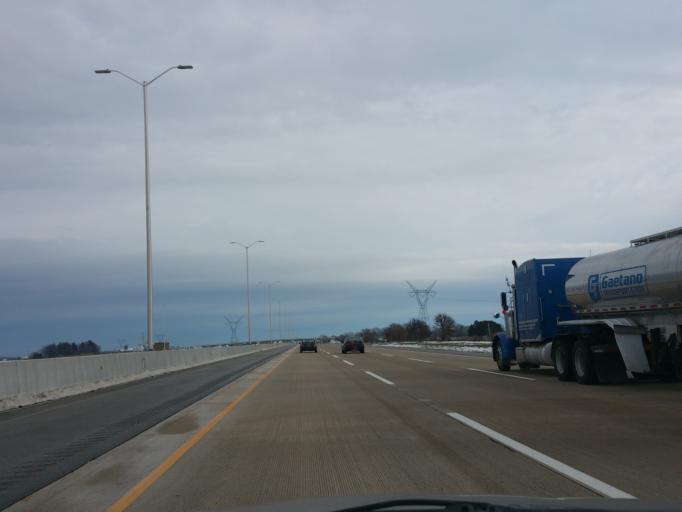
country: US
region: Illinois
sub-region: McHenry County
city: Marengo
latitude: 42.2092
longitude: -88.7142
